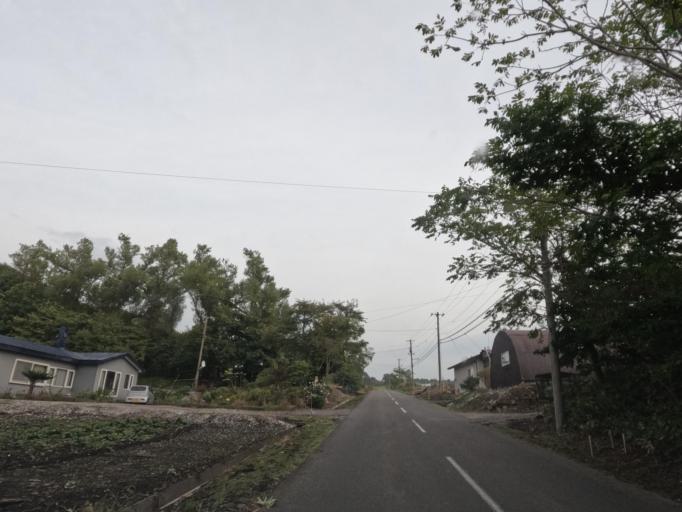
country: JP
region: Hokkaido
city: Date
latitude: 42.4103
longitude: 140.9165
